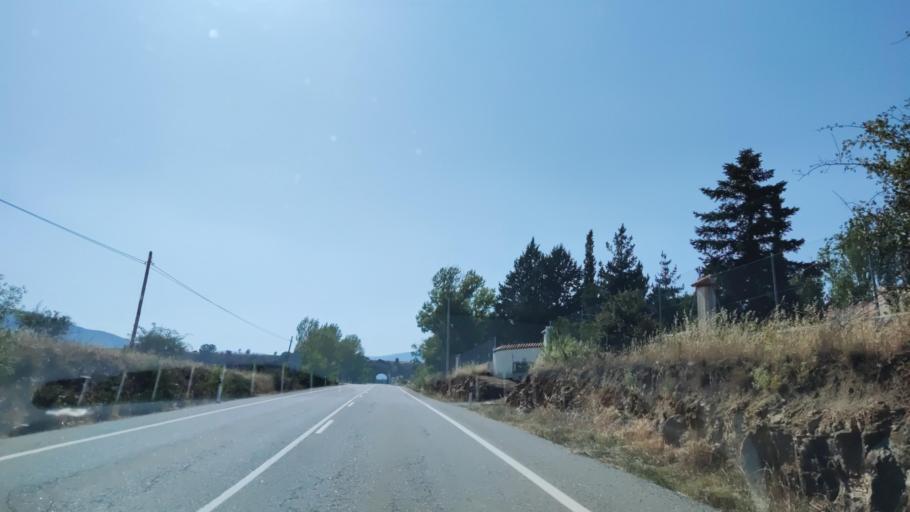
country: ES
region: Madrid
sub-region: Provincia de Madrid
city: Canencia
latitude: 40.9440
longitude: -3.7186
